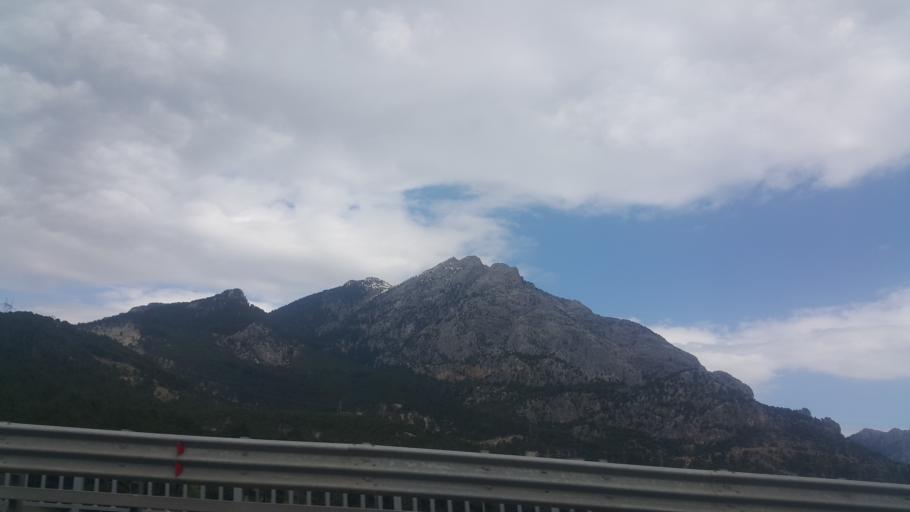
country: TR
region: Adana
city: Pozanti
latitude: 37.4106
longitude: 34.8825
